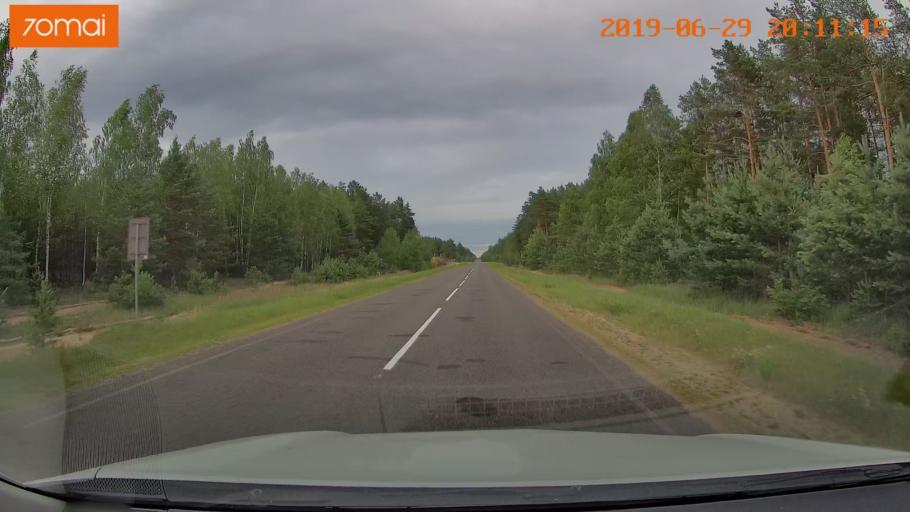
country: BY
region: Brest
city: Lahishyn
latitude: 52.3575
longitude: 26.1098
